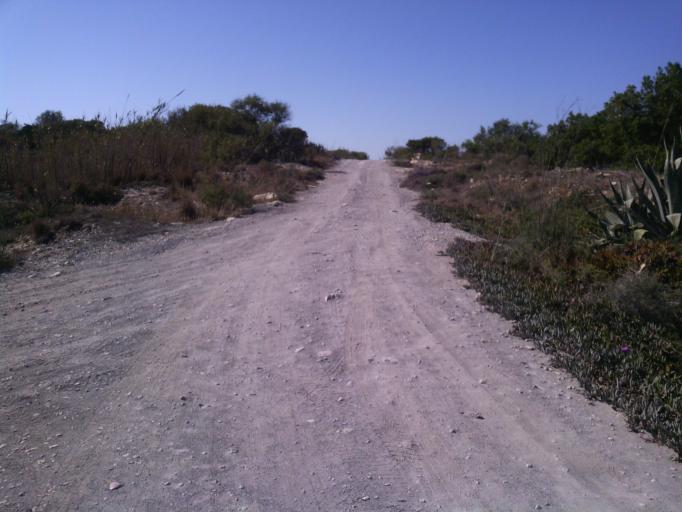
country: MT
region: Il-Mellieha
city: Mellieha
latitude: 35.9831
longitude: 14.3632
